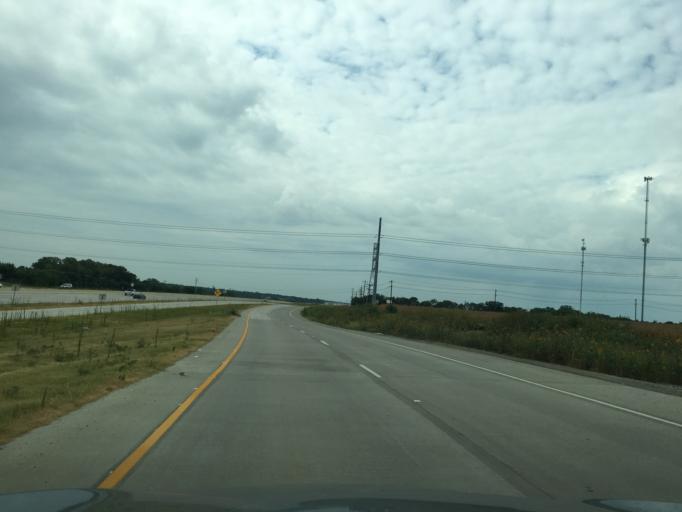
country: US
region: Texas
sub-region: Collin County
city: Melissa
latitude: 33.3181
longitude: -96.5912
